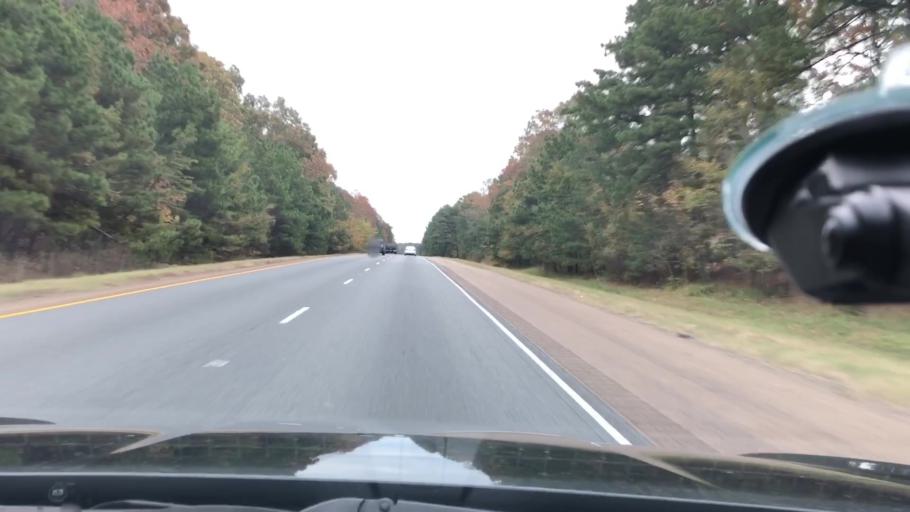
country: US
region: Arkansas
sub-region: Clark County
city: Gurdon
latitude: 33.9377
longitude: -93.2490
